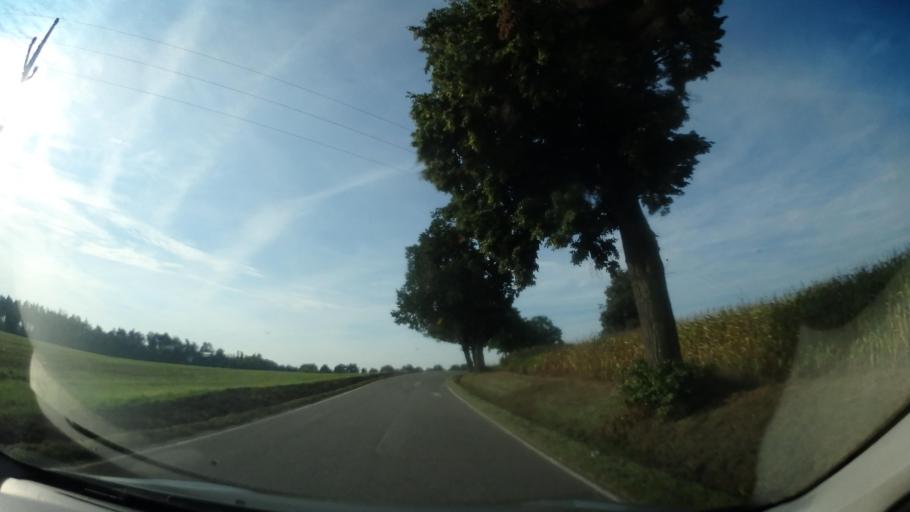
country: CZ
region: Jihocesky
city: Cimelice
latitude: 49.4686
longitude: 14.1506
